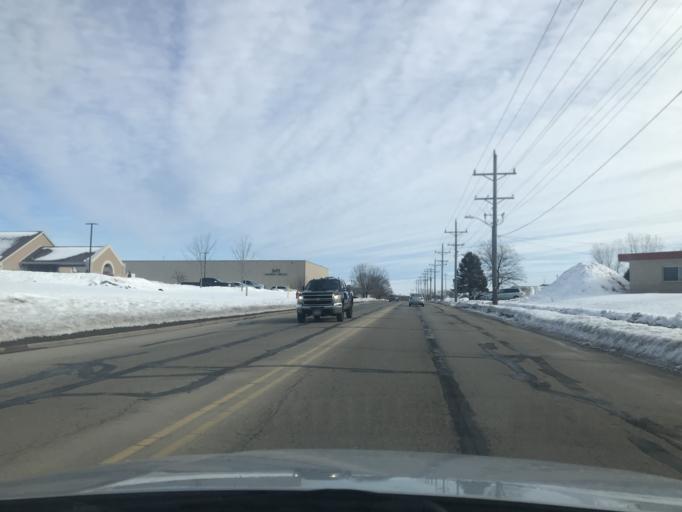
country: US
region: Wisconsin
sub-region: Oconto County
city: Oconto Falls
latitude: 44.8827
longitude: -88.1500
